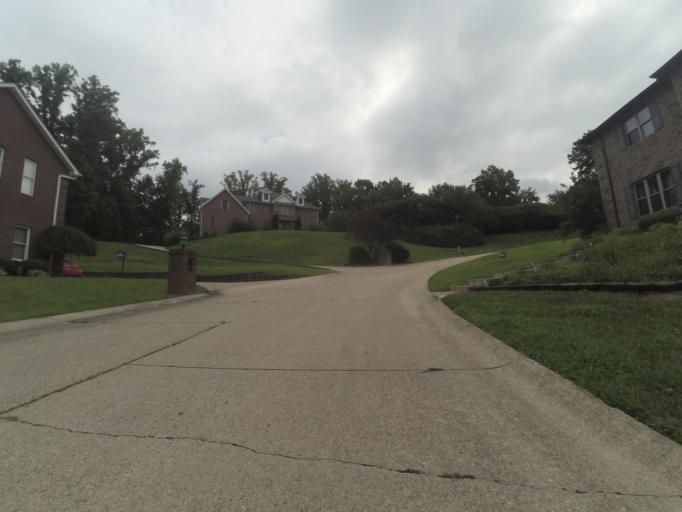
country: US
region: West Virginia
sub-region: Cabell County
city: Huntington
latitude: 38.3999
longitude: -82.3990
